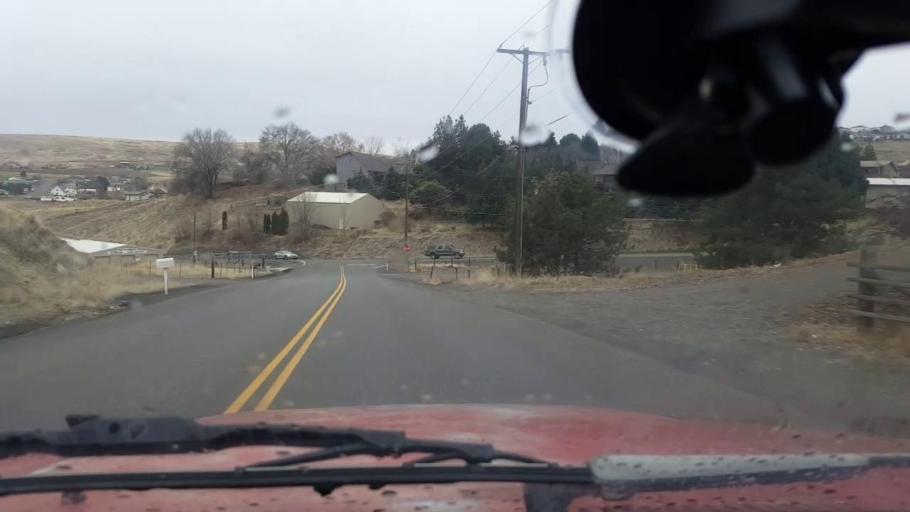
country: US
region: Washington
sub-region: Asotin County
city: Clarkston Heights-Vineland
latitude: 46.3787
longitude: -117.0858
